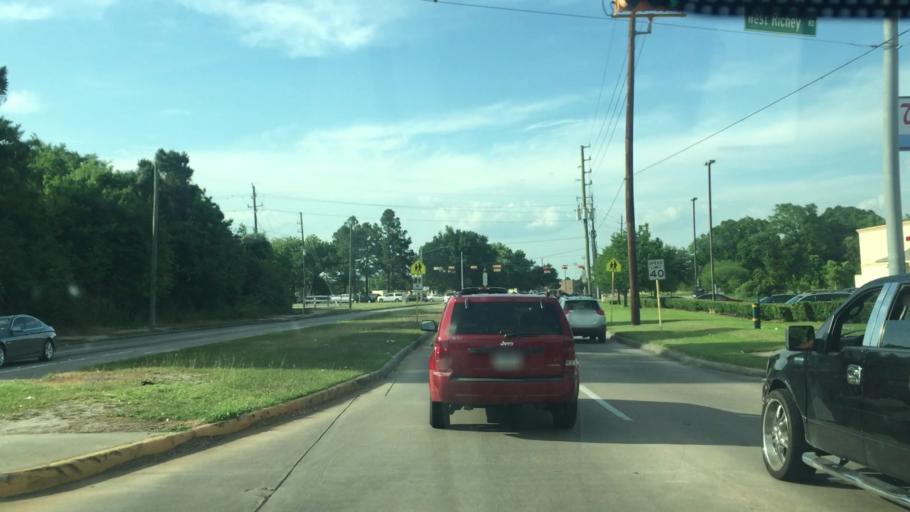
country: US
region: Texas
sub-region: Harris County
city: Hudson
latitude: 29.9614
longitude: -95.4985
